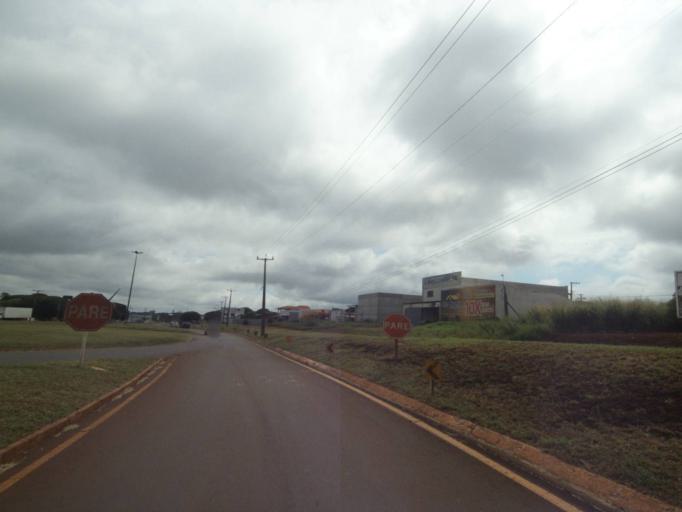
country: BR
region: Parana
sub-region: Campo Mourao
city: Campo Mourao
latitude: -24.0204
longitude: -52.3635
